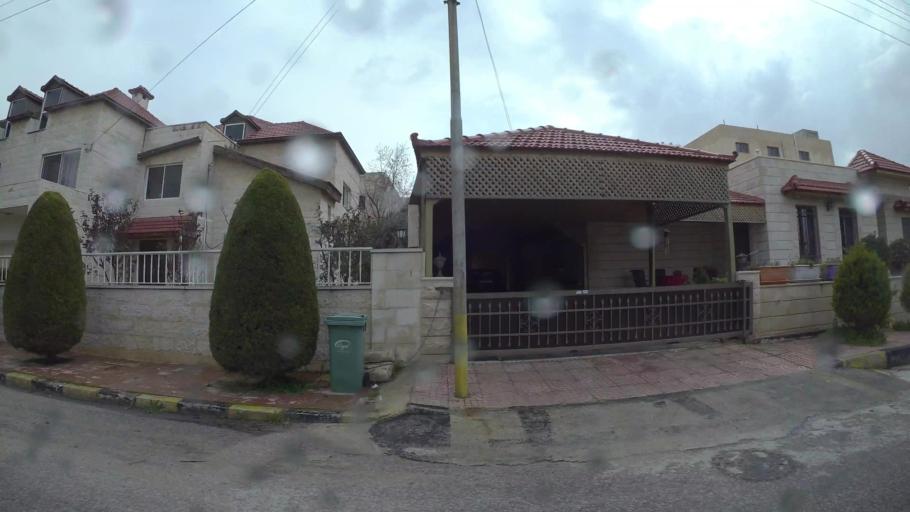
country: JO
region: Amman
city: Umm as Summaq
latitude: 31.8882
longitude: 35.8550
